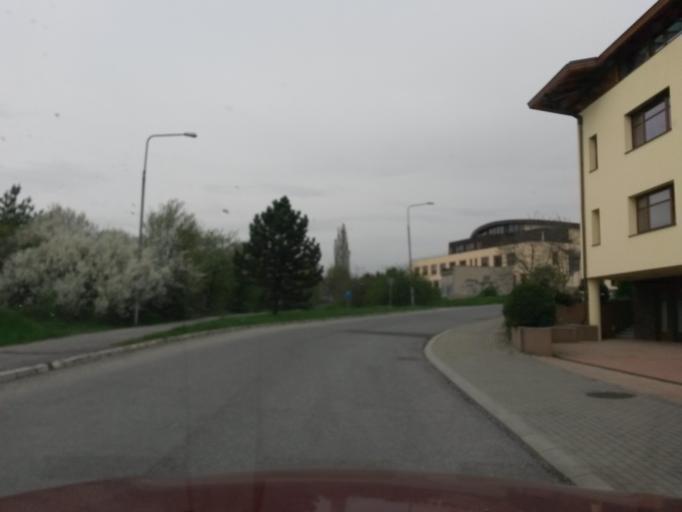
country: SK
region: Kosicky
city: Kosice
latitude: 48.7113
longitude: 21.2215
